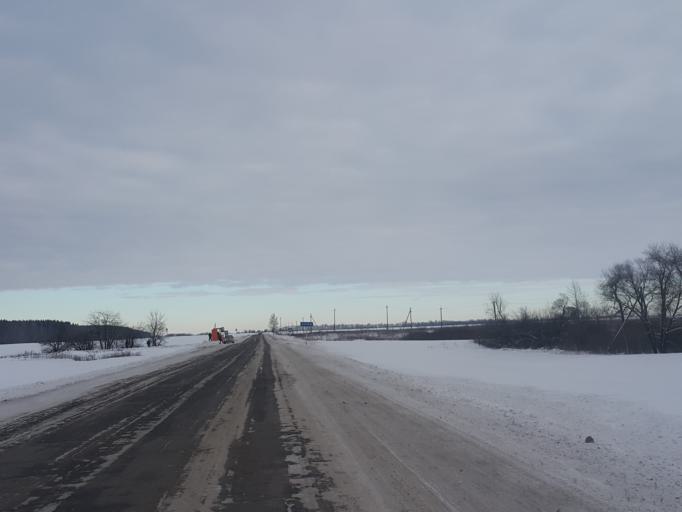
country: RU
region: Tambov
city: Novaya Lyada
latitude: 52.7518
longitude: 41.7163
